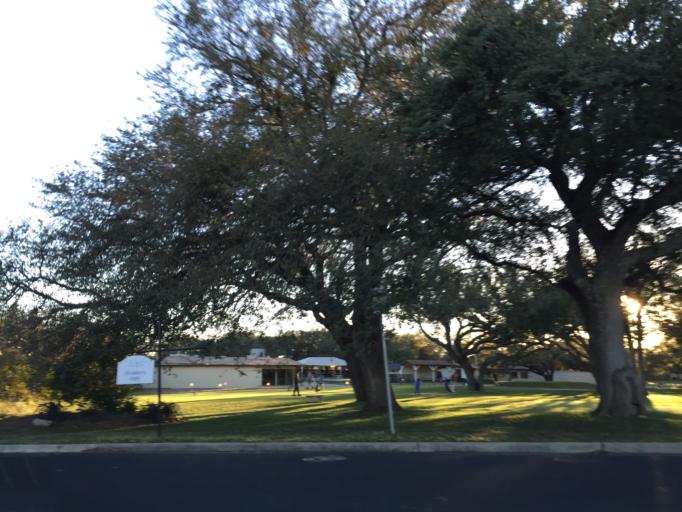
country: US
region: Texas
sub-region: Williamson County
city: Jollyville
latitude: 30.4383
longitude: -97.7810
